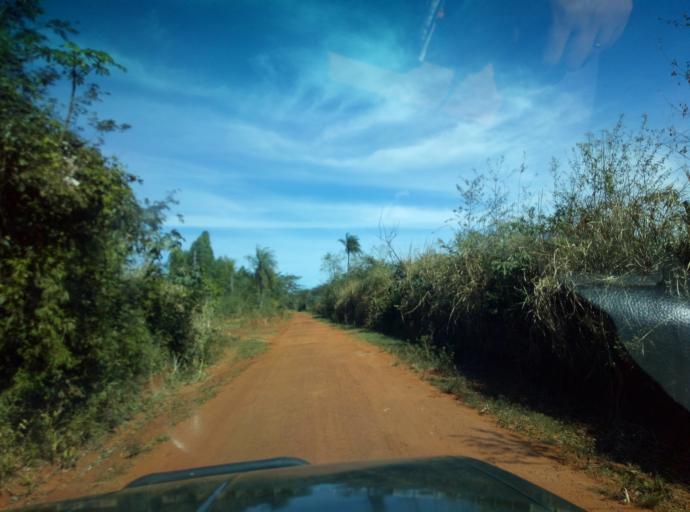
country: PY
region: Caaguazu
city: Doctor Cecilio Baez
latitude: -25.1814
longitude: -56.2541
